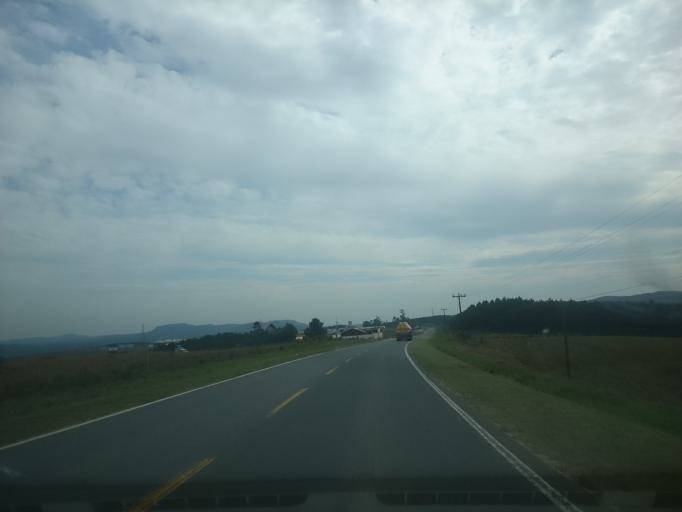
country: BR
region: Santa Catarina
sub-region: Lages
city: Lages
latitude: -27.7647
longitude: -50.3284
